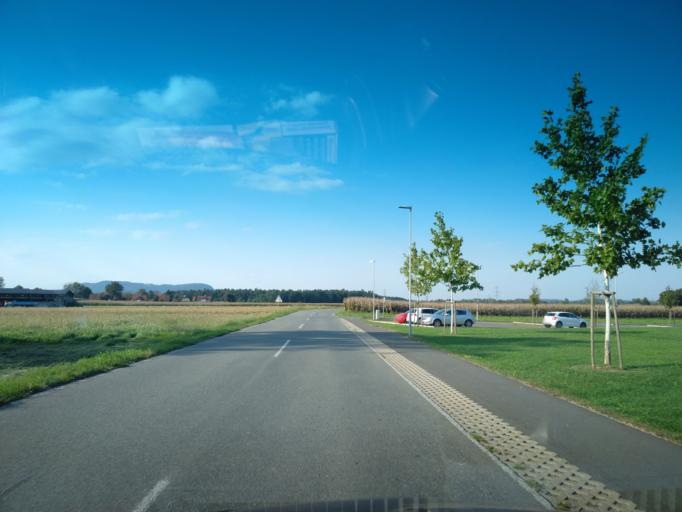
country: AT
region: Styria
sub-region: Politischer Bezirk Leibnitz
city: Kaindorf an der Sulm
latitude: 46.8164
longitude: 15.5567
